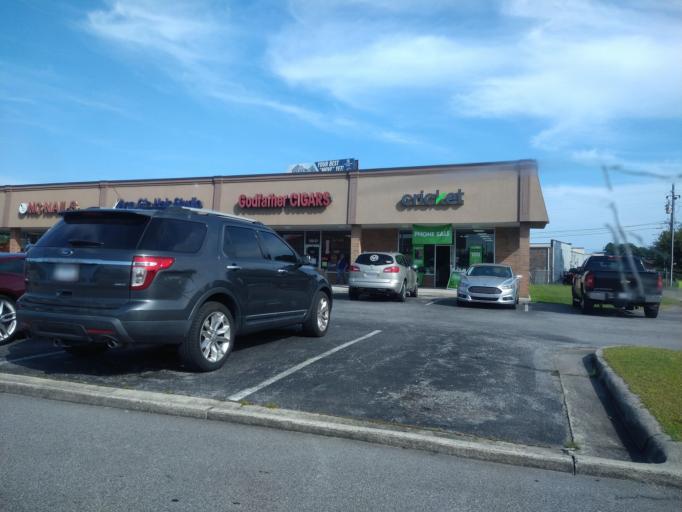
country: US
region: North Carolina
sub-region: Onslow County
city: Pumpkin Center
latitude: 34.7736
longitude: -77.3895
